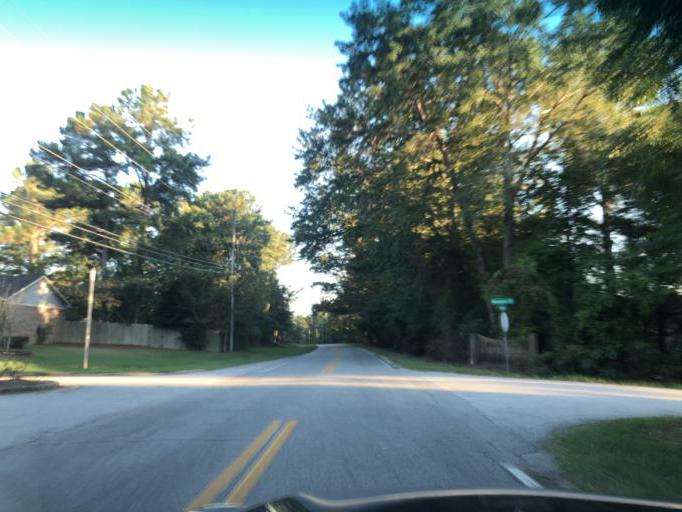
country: US
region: Georgia
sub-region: Muscogee County
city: Columbus
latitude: 32.5381
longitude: -84.8934
